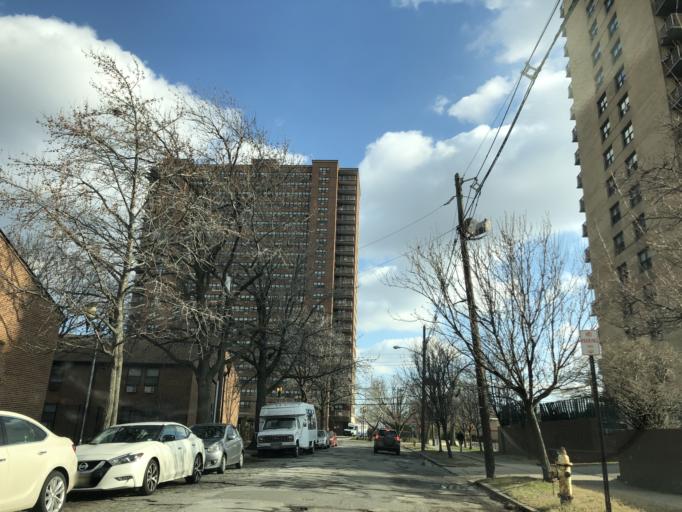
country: US
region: New Jersey
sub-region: Camden County
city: Camden
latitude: 39.9495
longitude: -75.1173
